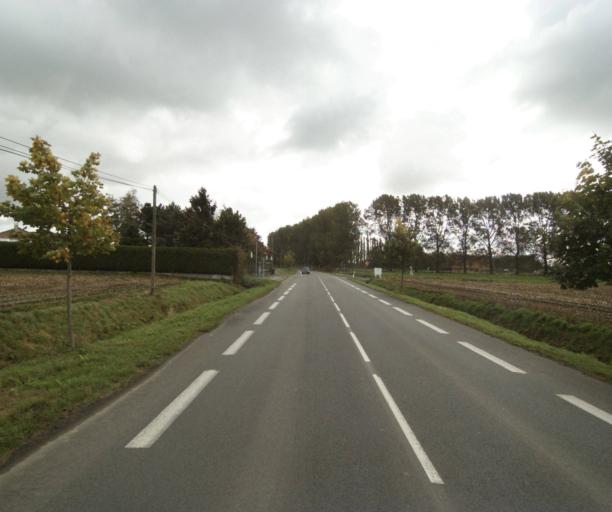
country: FR
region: Nord-Pas-de-Calais
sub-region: Departement du Nord
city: Quesnoy-sur-Deule
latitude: 50.7004
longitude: 3.0104
